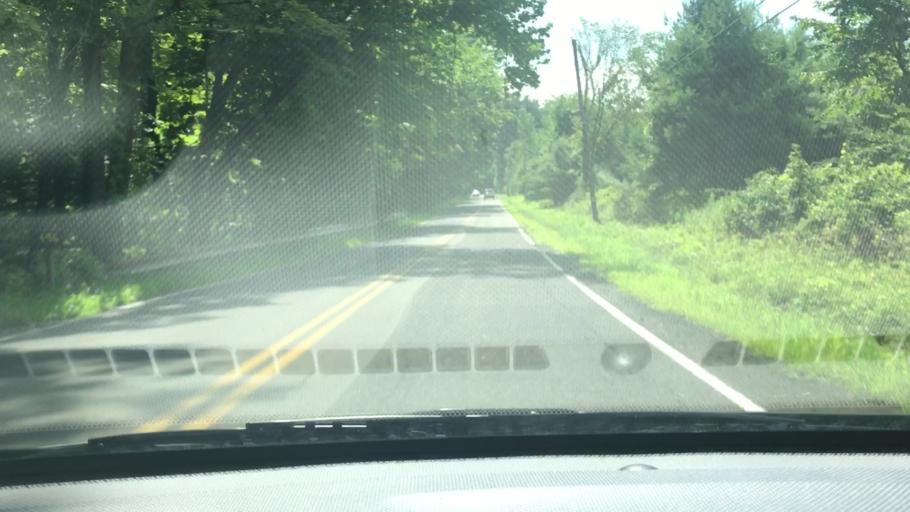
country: US
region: New York
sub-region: Ulster County
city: Stone Ridge
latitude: 41.8826
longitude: -74.1488
